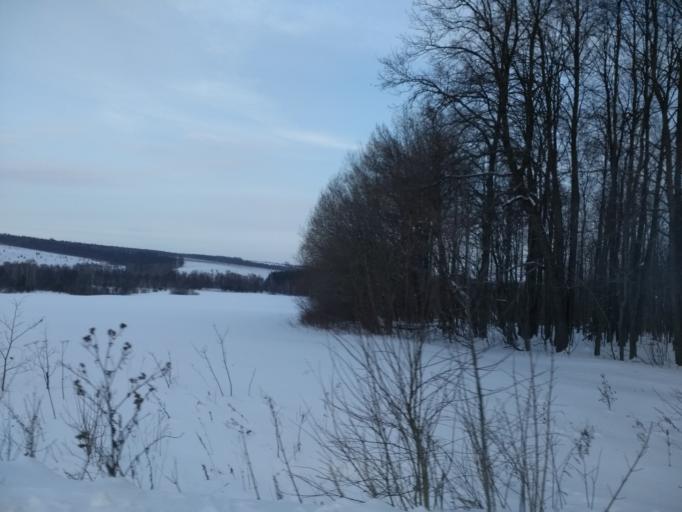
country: RU
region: Bashkortostan
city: Kudeyevskiy
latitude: 54.7153
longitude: 56.6332
